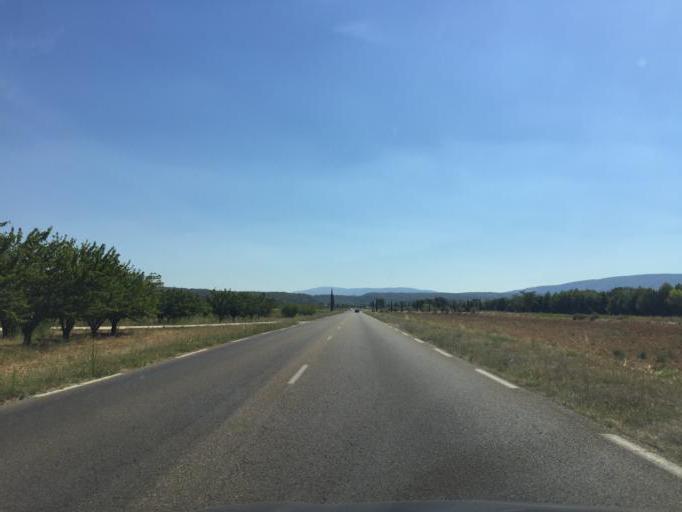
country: FR
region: Provence-Alpes-Cote d'Azur
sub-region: Departement du Vaucluse
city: Oppede
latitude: 43.8630
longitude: 5.1736
